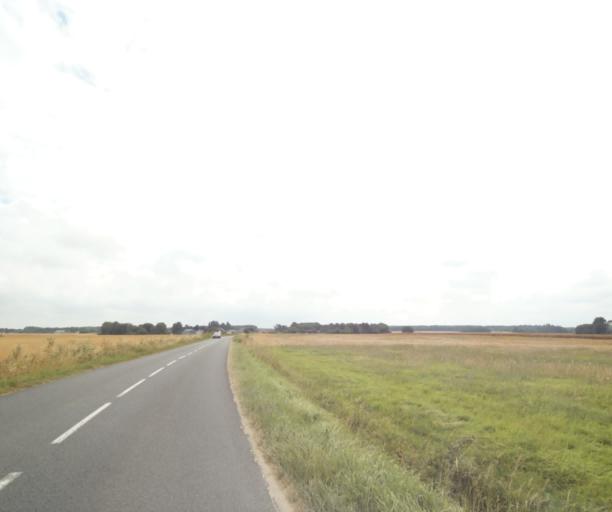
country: FR
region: Centre
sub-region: Departement du Loiret
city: Boigny-sur-Bionne
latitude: 47.9321
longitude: 2.0361
